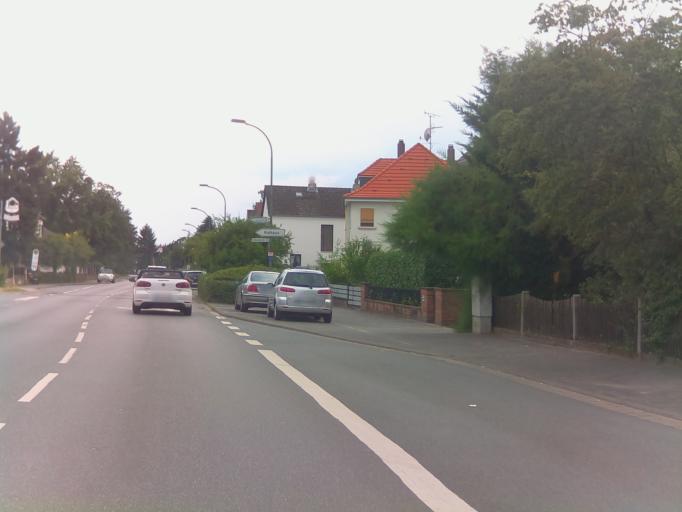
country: DE
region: Hesse
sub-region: Regierungsbezirk Darmstadt
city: Bickenbach
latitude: 49.7446
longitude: 8.6212
